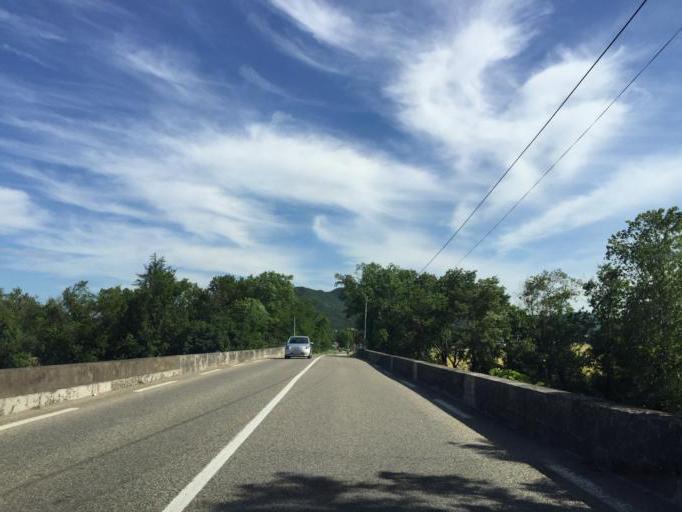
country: FR
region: Rhone-Alpes
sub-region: Departement de l'Ardeche
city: Le Pouzin
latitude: 44.7320
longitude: 4.7396
